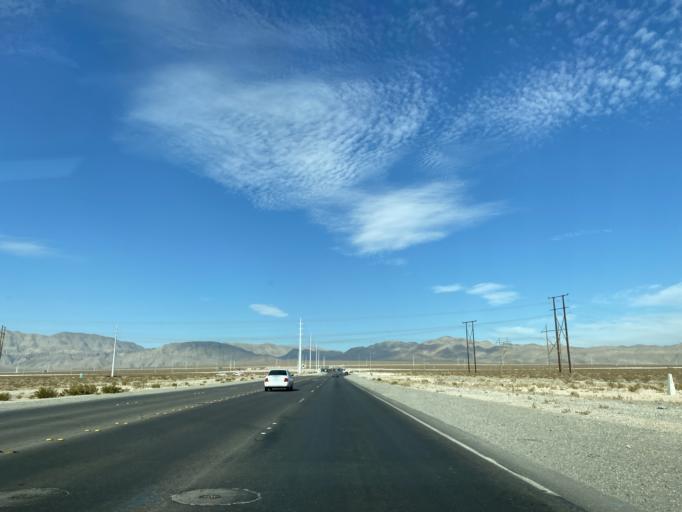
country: US
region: Nevada
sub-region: Clark County
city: Nellis Air Force Base
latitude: 36.2802
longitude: -115.0799
